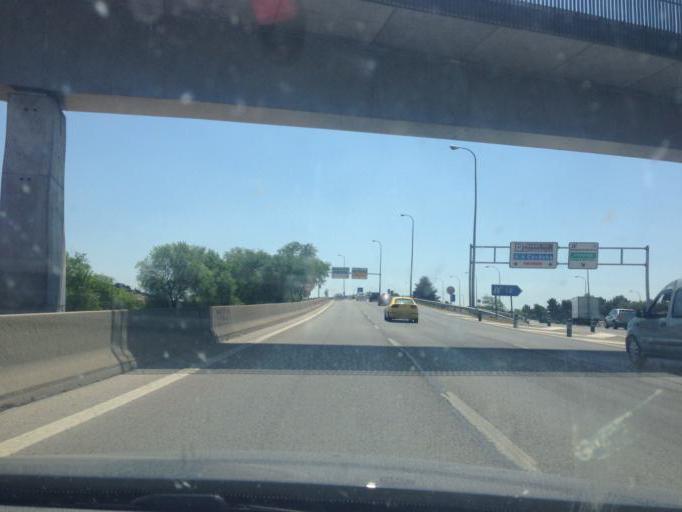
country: ES
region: Madrid
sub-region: Provincia de Madrid
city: Usera
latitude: 40.3838
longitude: -3.6921
